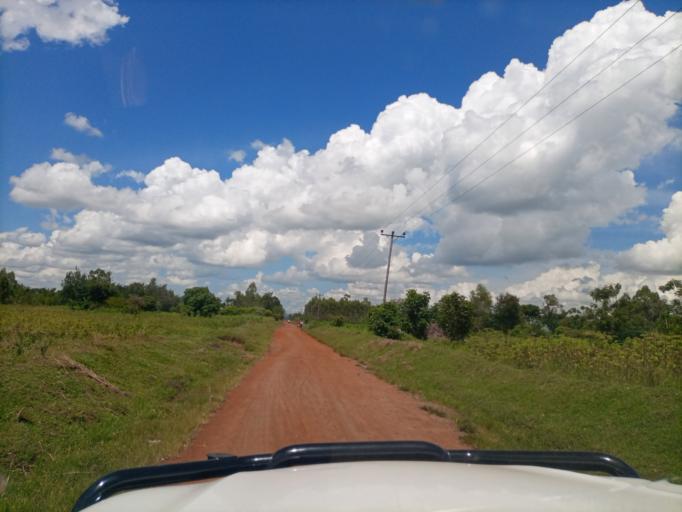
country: UG
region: Eastern Region
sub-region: Tororo District
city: Tororo
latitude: 0.6682
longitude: 34.0030
